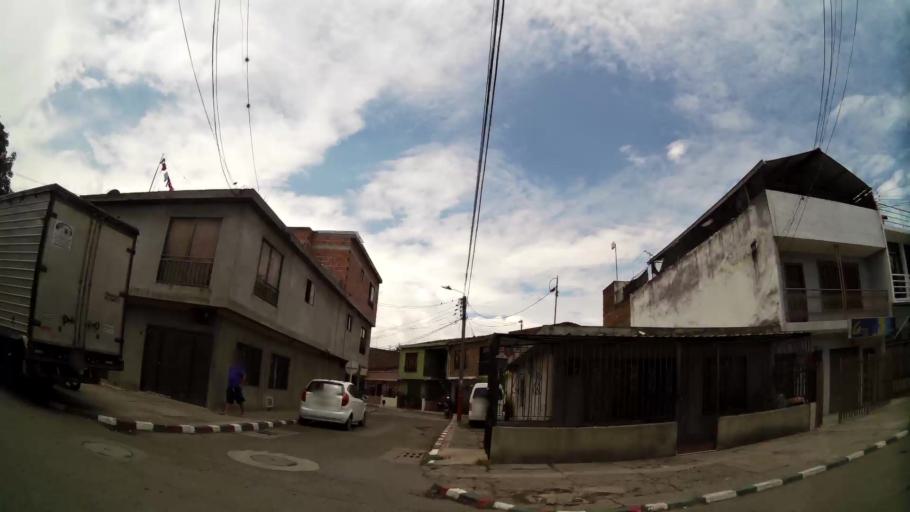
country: CO
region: Valle del Cauca
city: Cali
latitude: 3.4463
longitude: -76.4879
